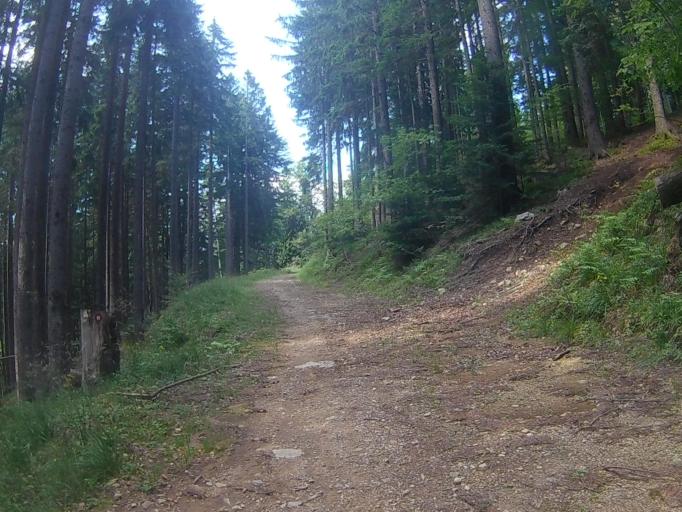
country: SI
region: Ruse
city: Ruse
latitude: 46.5051
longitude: 15.5396
